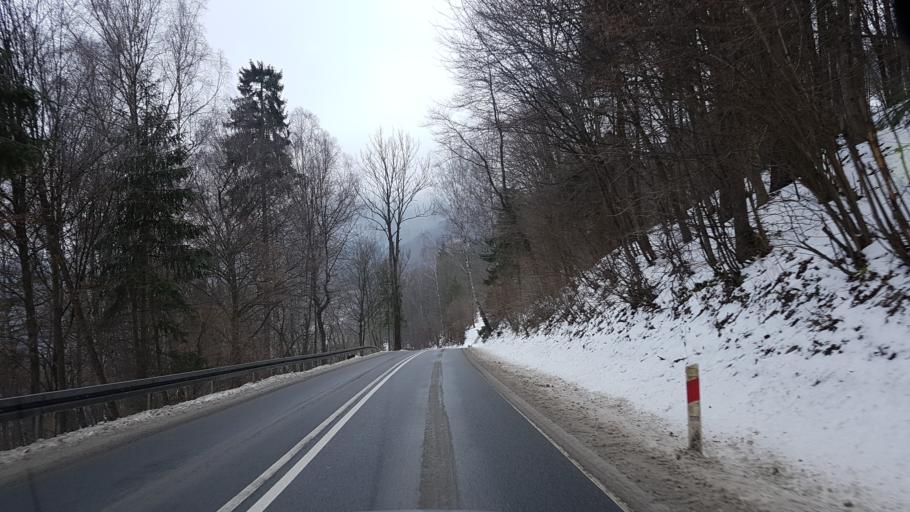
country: PL
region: Lesser Poland Voivodeship
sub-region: Powiat nowosadecki
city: Piwniczna-Zdroj
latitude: 49.4071
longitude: 20.7461
